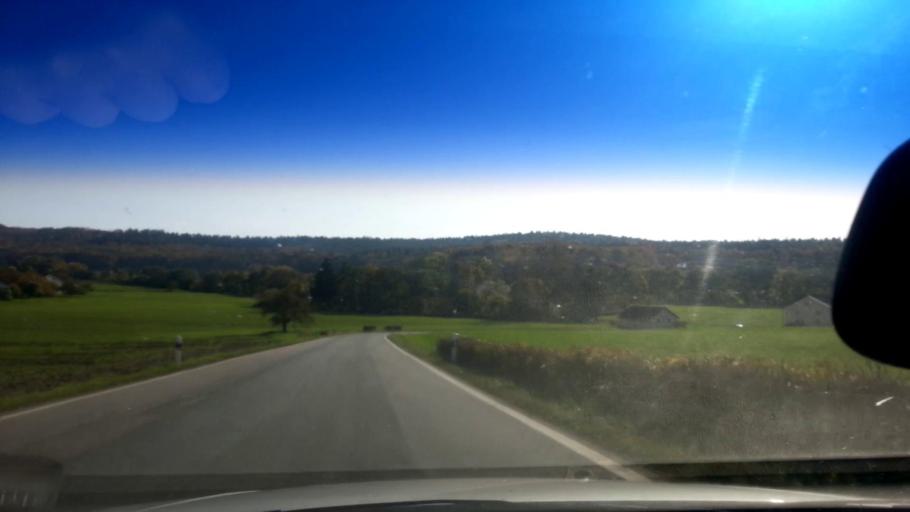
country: DE
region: Bavaria
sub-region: Upper Franconia
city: Litzendorf
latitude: 49.9389
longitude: 11.0161
